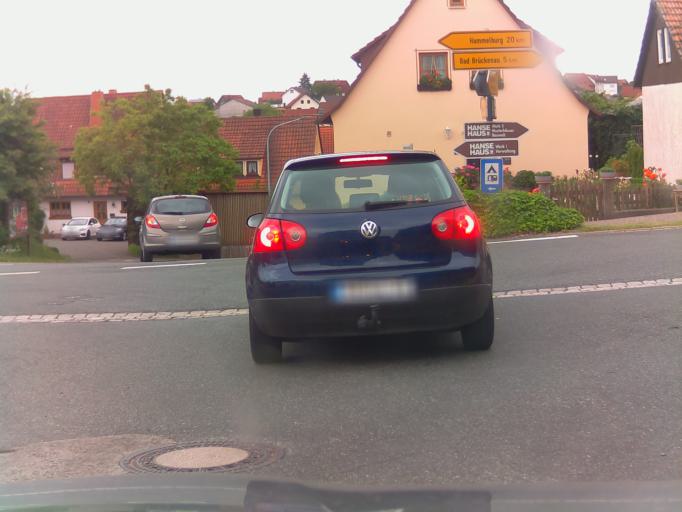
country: DE
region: Bavaria
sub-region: Regierungsbezirk Unterfranken
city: Oberleichtersbach
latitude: 50.2760
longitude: 9.8072
